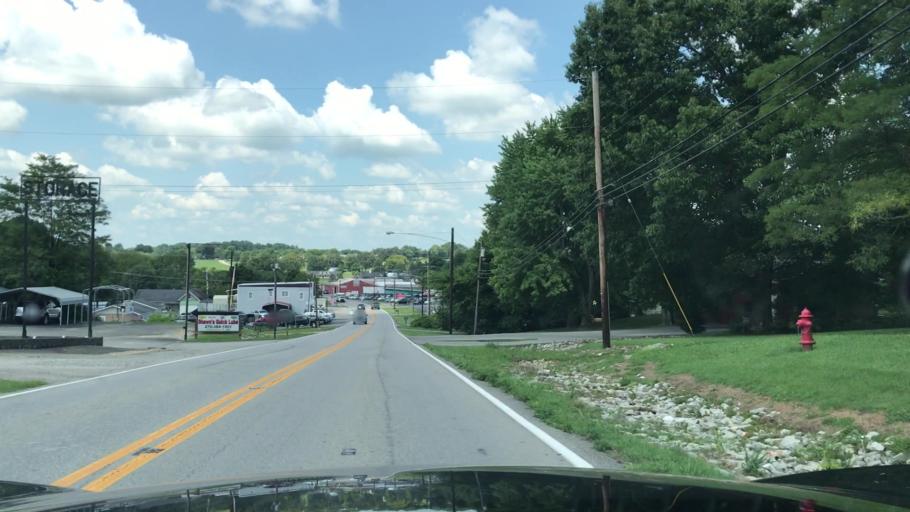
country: US
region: Kentucky
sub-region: Adair County
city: Columbia
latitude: 37.0995
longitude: -85.3161
